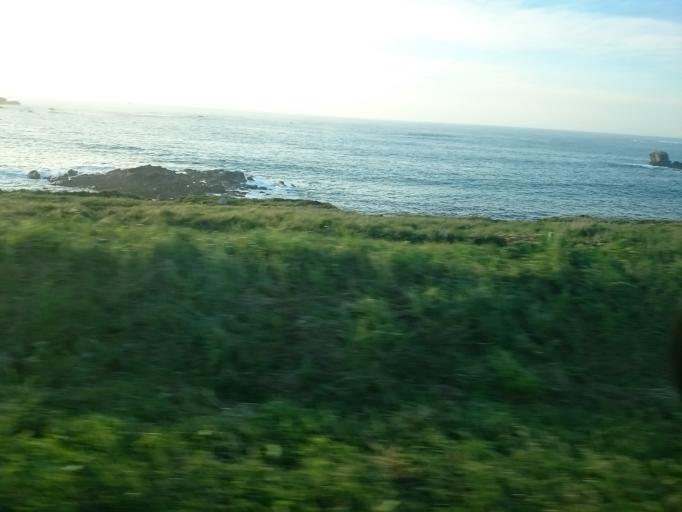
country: FR
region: Brittany
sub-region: Departement du Finistere
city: Landunvez
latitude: 48.5361
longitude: -4.7484
